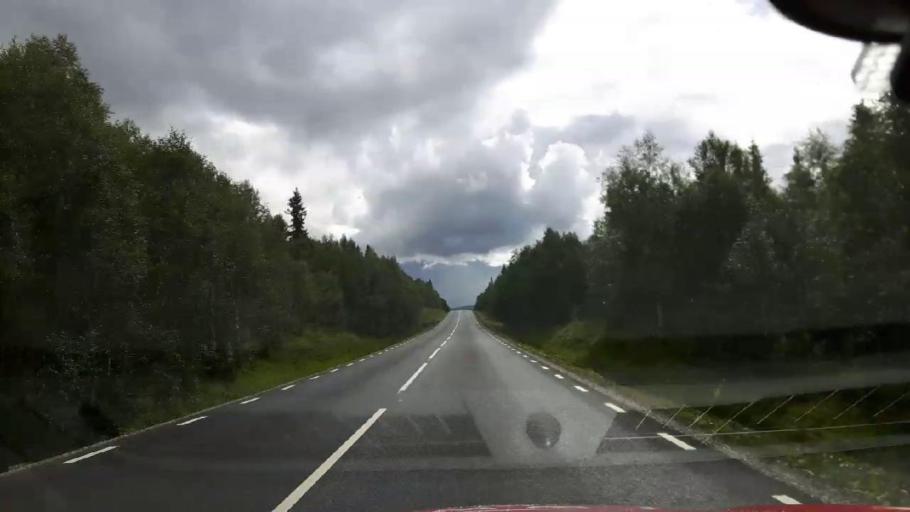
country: NO
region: Nord-Trondelag
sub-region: Royrvik
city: Royrvik
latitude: 64.8852
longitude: 14.2024
